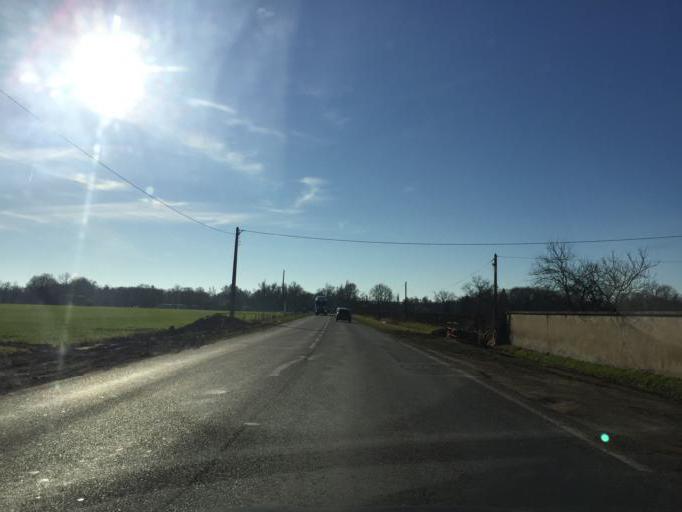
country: FR
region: Auvergne
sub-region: Departement de l'Allier
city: Saint-Remy-en-Rollat
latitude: 46.1679
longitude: 3.3954
